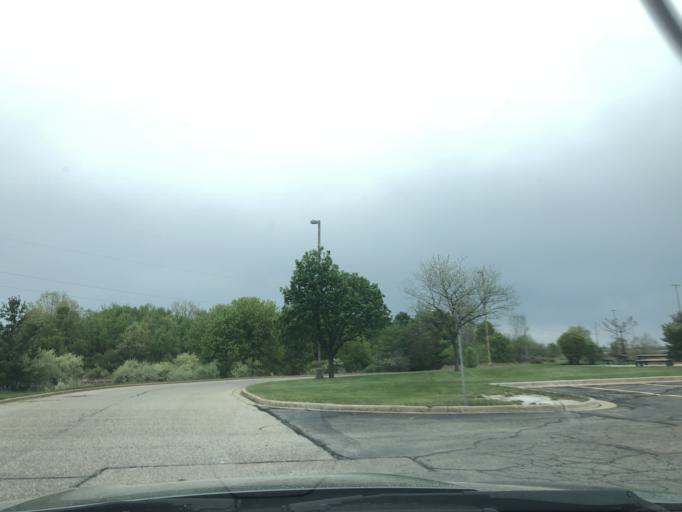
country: US
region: Michigan
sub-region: Eaton County
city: Dimondale
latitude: 42.6723
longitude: -84.6788
